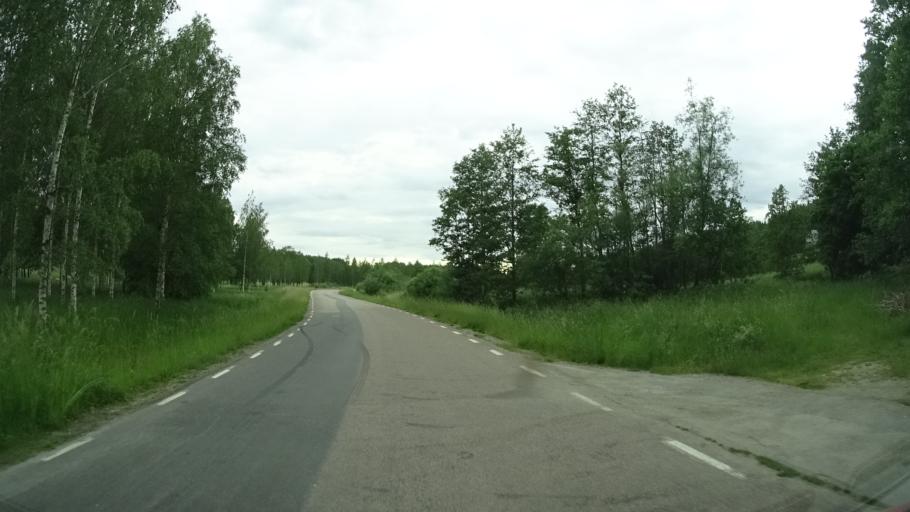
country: SE
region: Soedermanland
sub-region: Nykopings Kommun
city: Stigtomta
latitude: 58.7565
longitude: 16.7169
